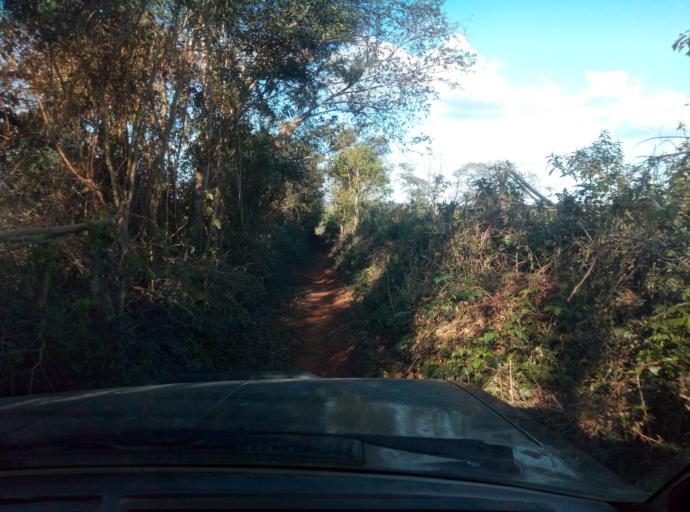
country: PY
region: Caaguazu
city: Carayao
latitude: -25.1756
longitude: -56.2646
